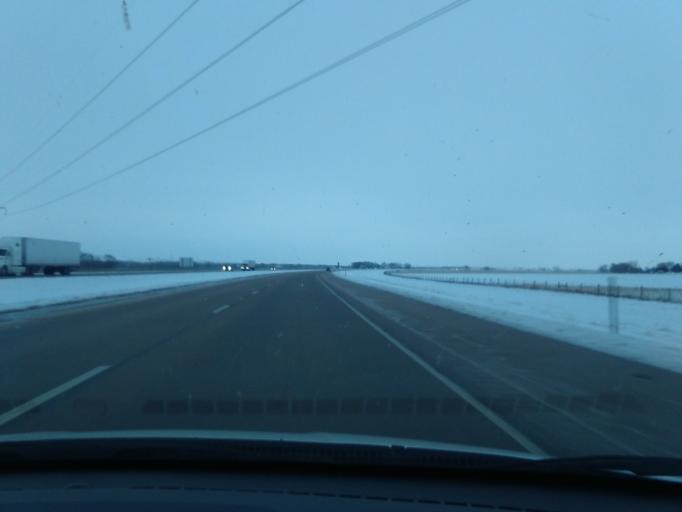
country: US
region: Nebraska
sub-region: Keith County
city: Ogallala
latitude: 41.1184
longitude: -101.6913
